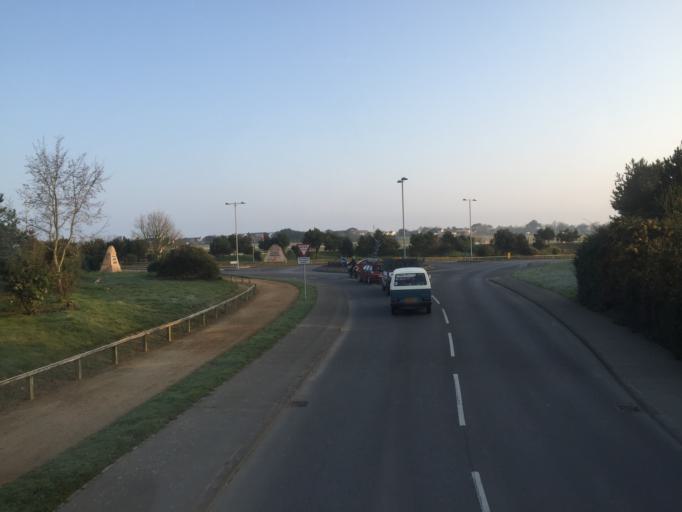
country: JE
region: St Helier
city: Saint Helier
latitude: 49.2056
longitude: -2.1900
